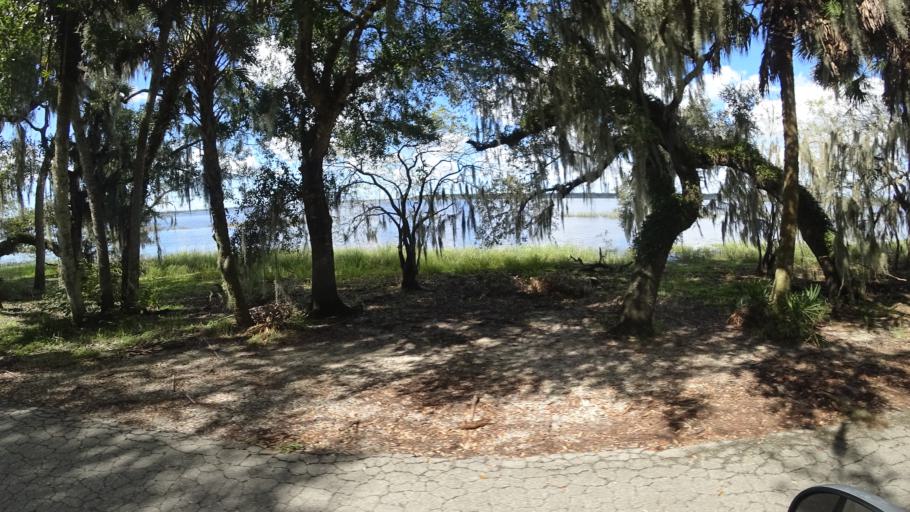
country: US
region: Florida
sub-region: Sarasota County
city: Lake Sarasota
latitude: 27.2736
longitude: -82.2713
